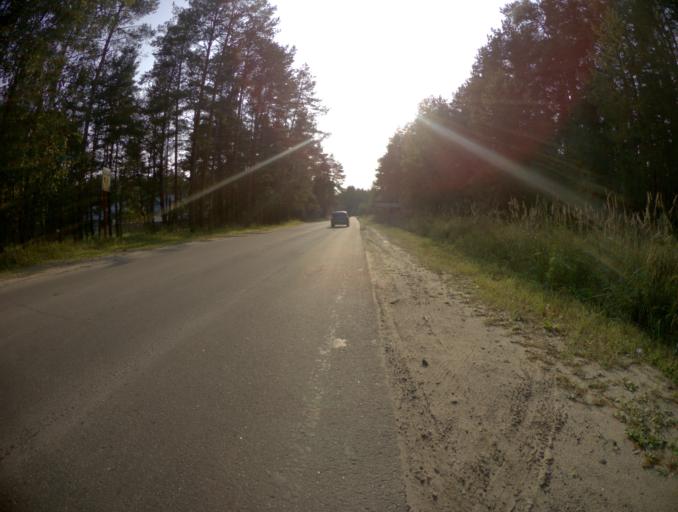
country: RU
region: Vladimir
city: Kommunar
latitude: 56.1232
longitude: 40.4680
